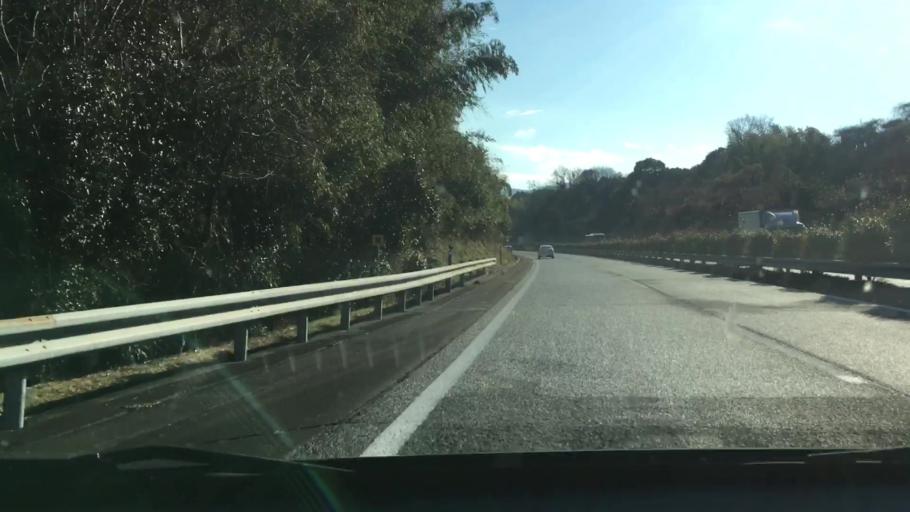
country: JP
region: Kumamoto
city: Hitoyoshi
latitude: 32.1916
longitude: 130.7772
